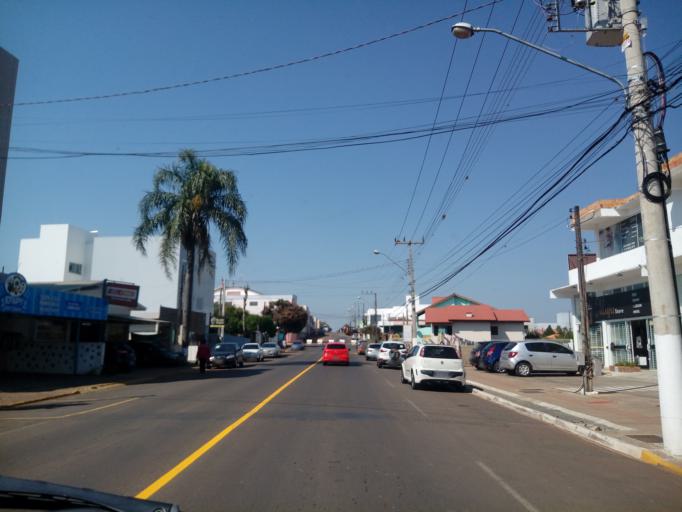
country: BR
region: Santa Catarina
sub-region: Chapeco
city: Chapeco
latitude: -27.0967
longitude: -52.6739
